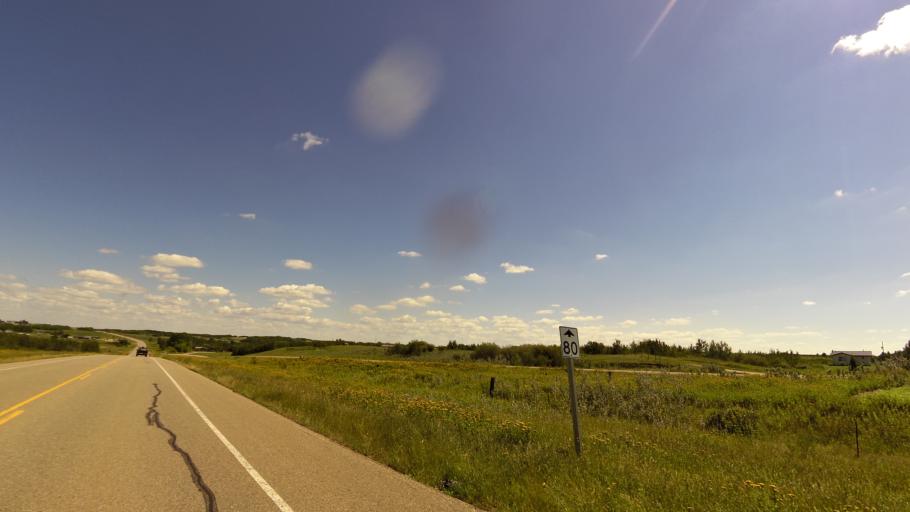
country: CA
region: Saskatchewan
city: Wilkie
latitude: 52.7553
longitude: -108.7414
